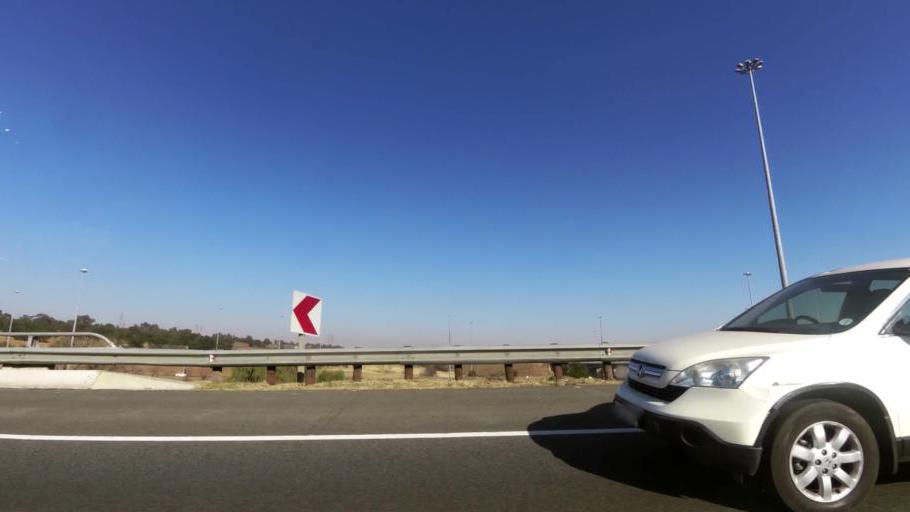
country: ZA
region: Gauteng
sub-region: City of Johannesburg Metropolitan Municipality
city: Johannesburg
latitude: -26.2588
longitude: 27.9653
